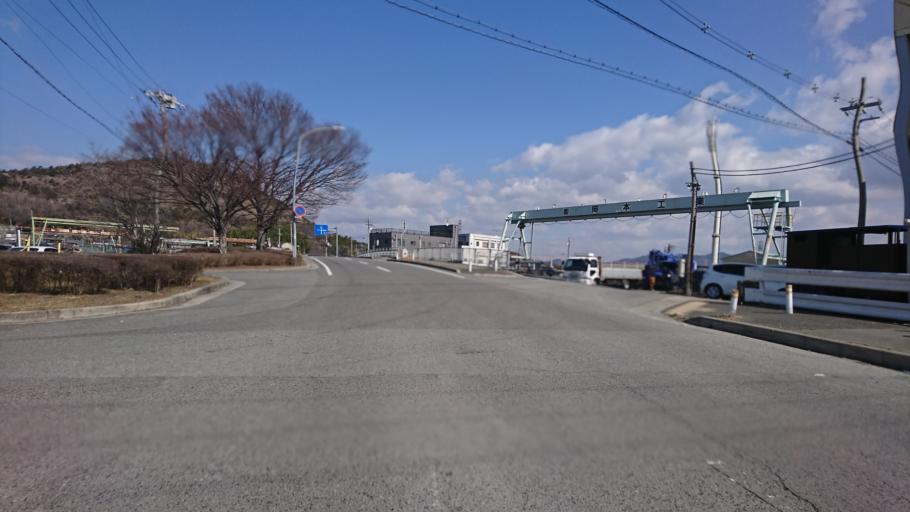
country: JP
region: Hyogo
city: Kakogawacho-honmachi
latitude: 34.7944
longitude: 134.8071
